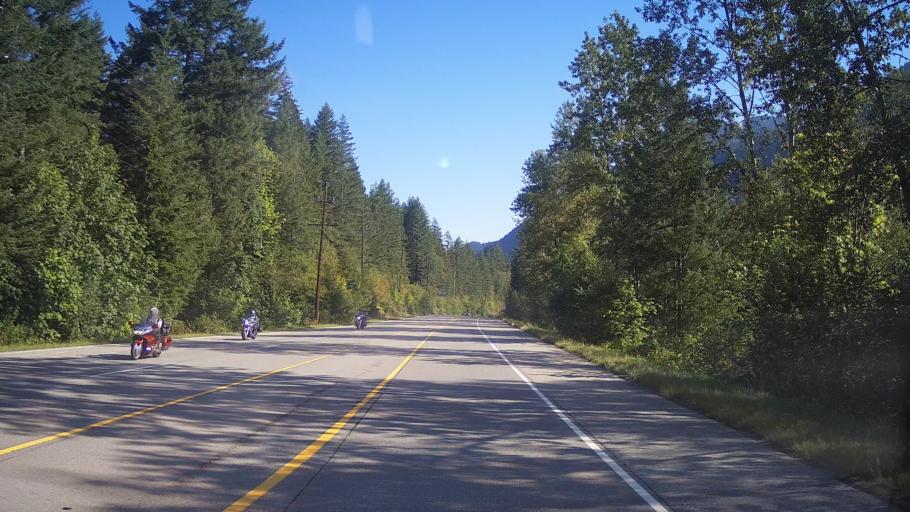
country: CA
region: British Columbia
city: Hope
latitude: 49.5019
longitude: -121.4198
